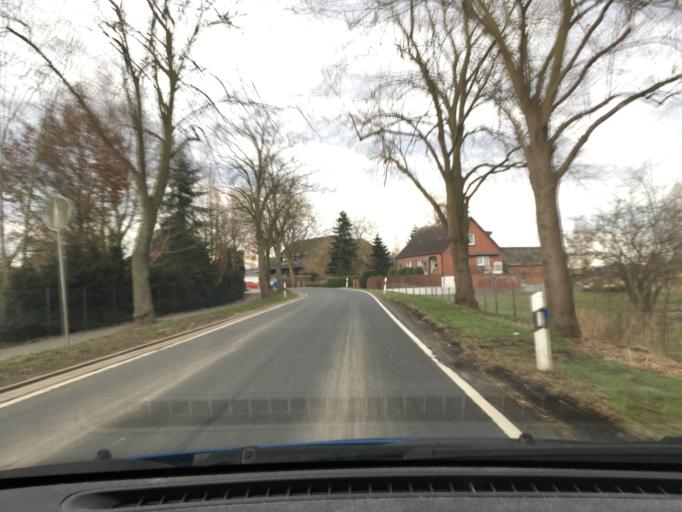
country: DE
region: Lower Saxony
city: Drage
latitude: 53.3748
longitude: 10.2568
